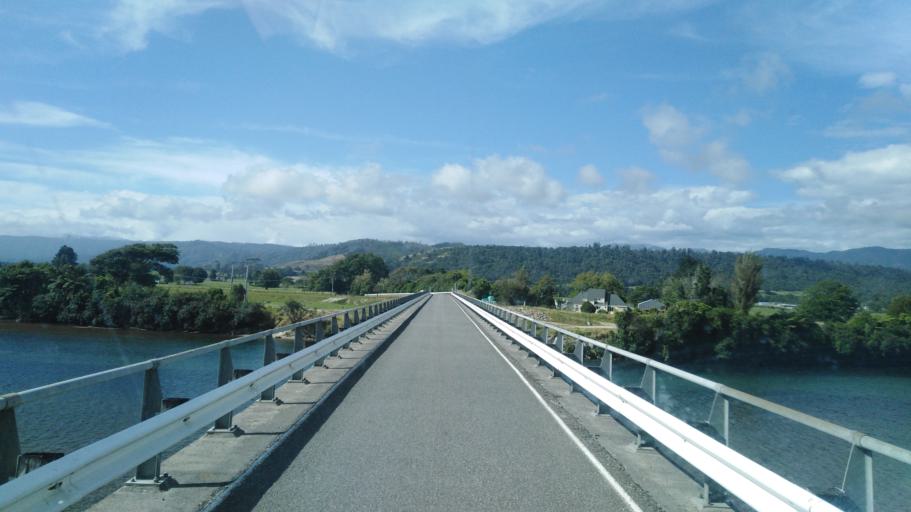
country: NZ
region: West Coast
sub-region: Buller District
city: Westport
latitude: -41.2614
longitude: 172.1308
